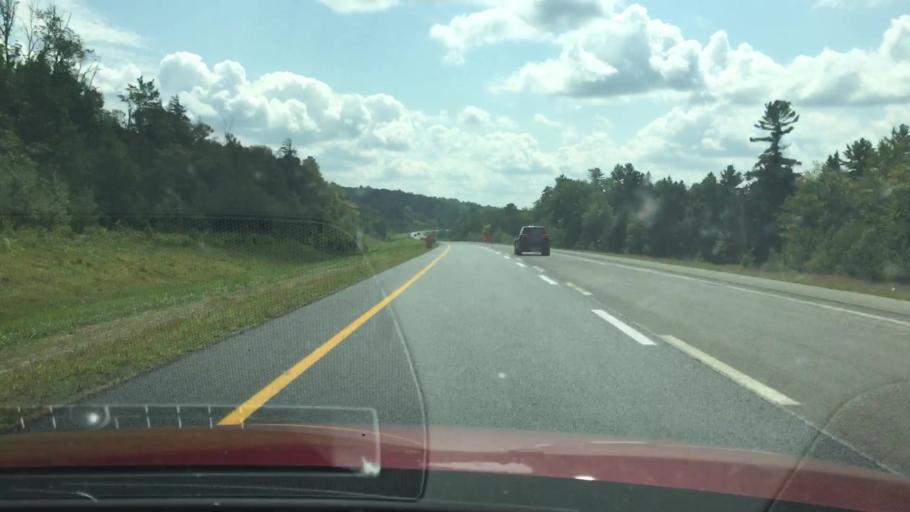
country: US
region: Maine
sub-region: Penobscot County
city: Medway
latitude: 45.7199
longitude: -68.4753
